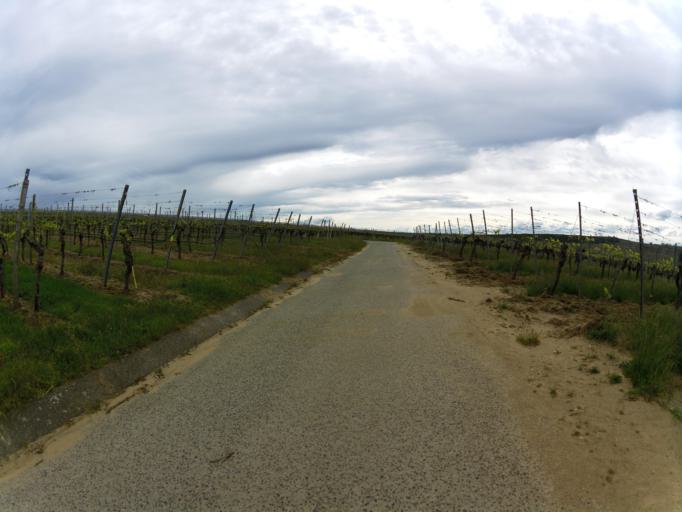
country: DE
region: Bavaria
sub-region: Regierungsbezirk Unterfranken
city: Nordheim
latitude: 49.8512
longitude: 10.1987
